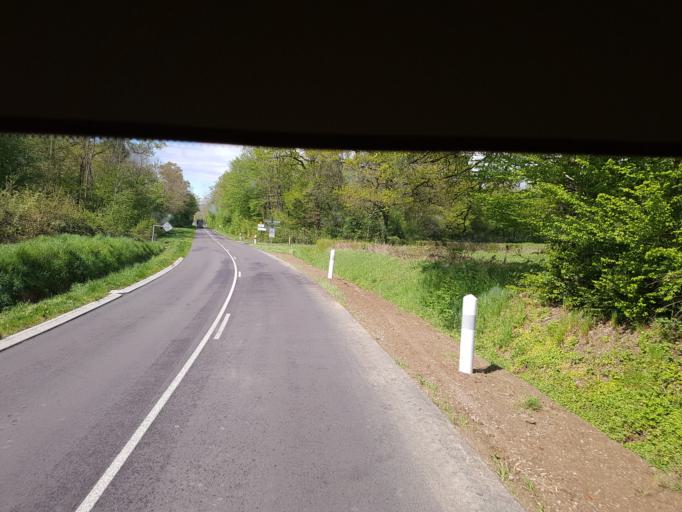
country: FR
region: Bourgogne
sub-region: Departement de Saone-et-Loire
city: Etang-sur-Arroux
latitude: 46.8518
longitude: 4.1977
